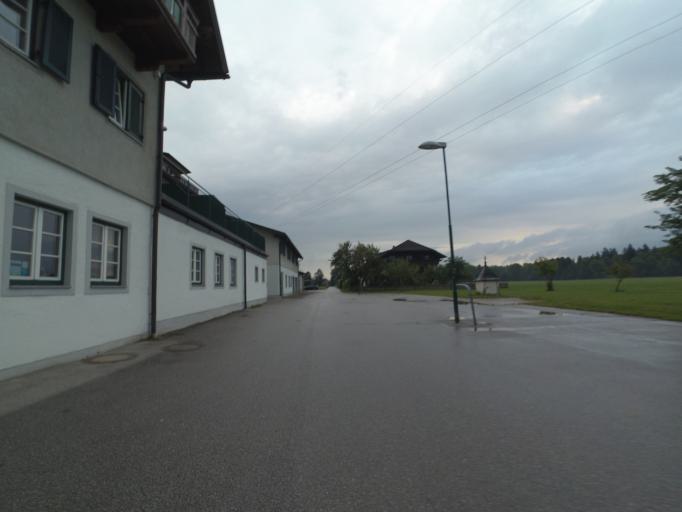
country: AT
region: Salzburg
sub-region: Politischer Bezirk Salzburg-Umgebung
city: Grodig
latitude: 47.7547
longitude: 13.0343
